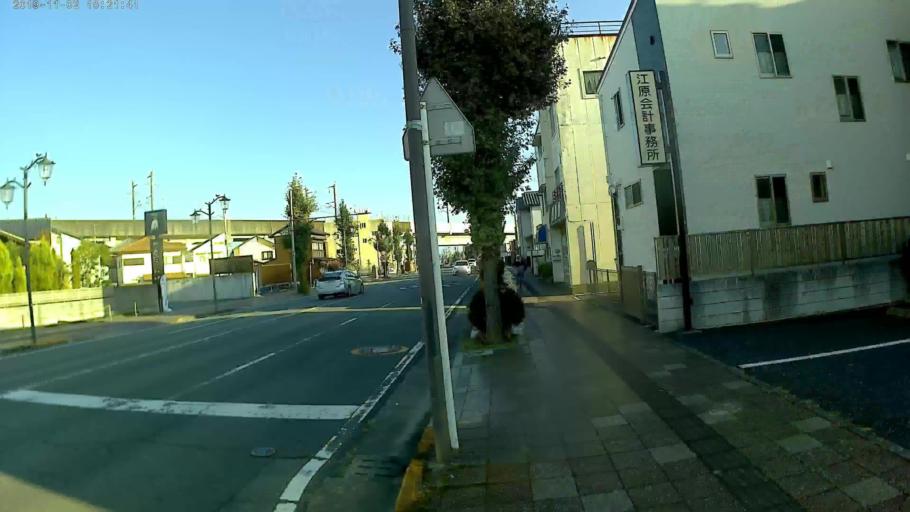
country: JP
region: Gunma
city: Takasaki
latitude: 36.3150
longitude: 139.0128
